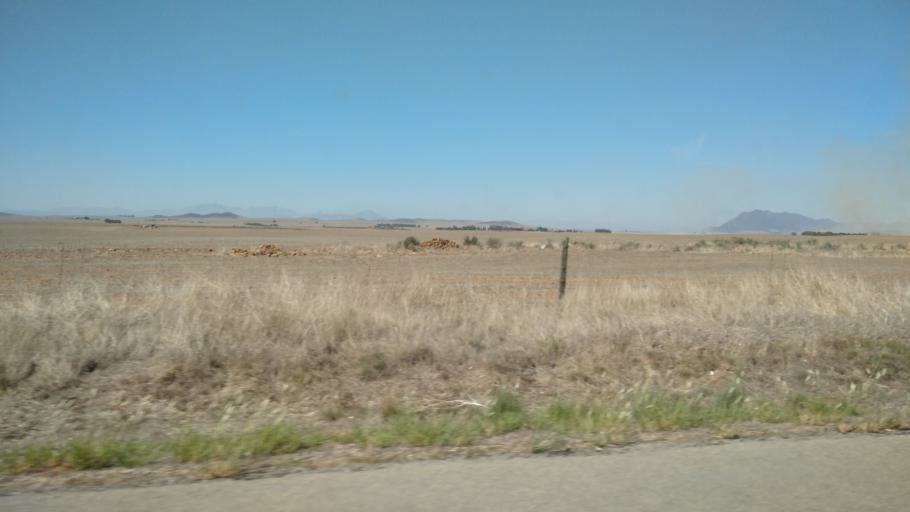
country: ZA
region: Western Cape
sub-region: West Coast District Municipality
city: Moorreesburg
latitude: -33.2798
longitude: 18.6030
